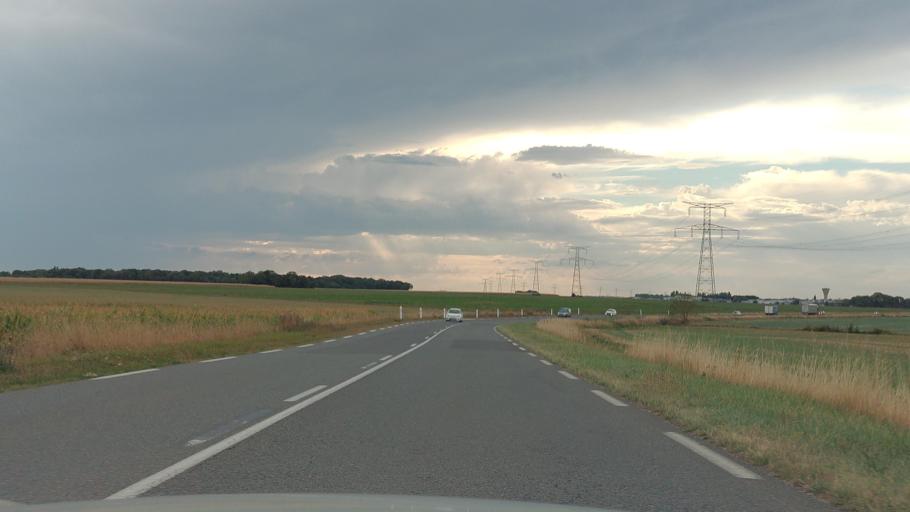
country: FR
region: Ile-de-France
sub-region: Departement de Seine-et-Marne
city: Guignes
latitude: 48.6220
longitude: 2.8331
